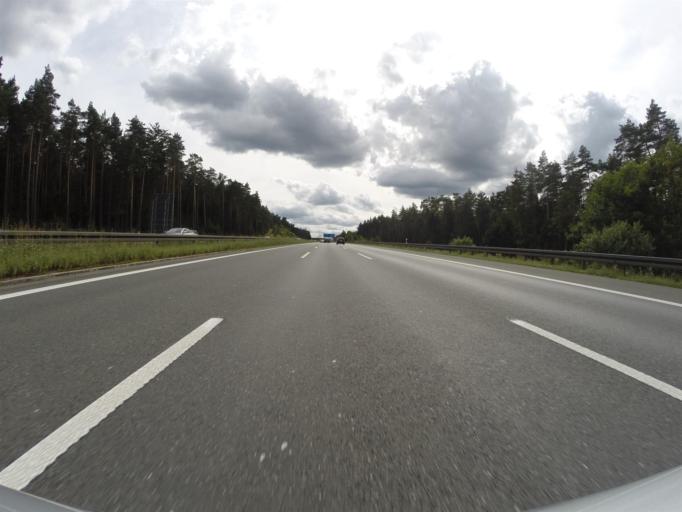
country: DE
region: Bavaria
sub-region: Upper Franconia
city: Pegnitz
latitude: 49.7133
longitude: 11.4742
